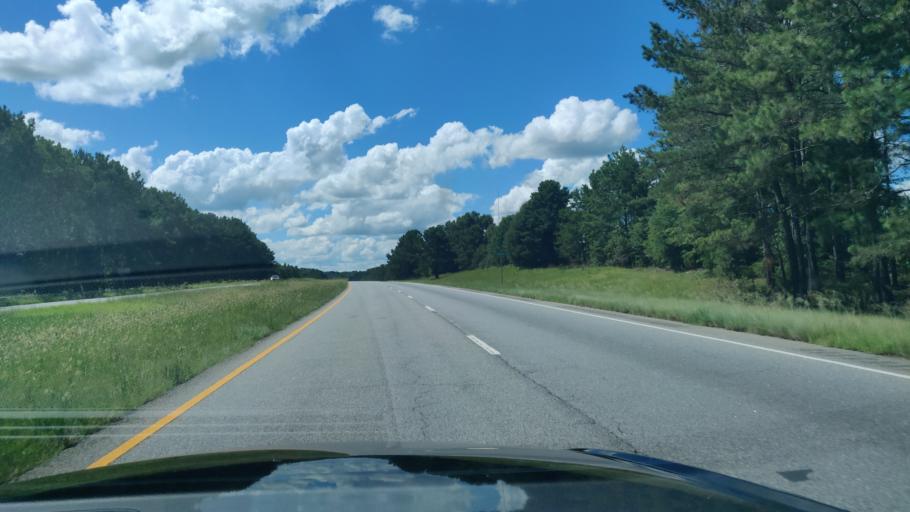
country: US
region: Georgia
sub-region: Chattahoochee County
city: Cusseta
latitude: 32.2912
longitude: -84.7680
